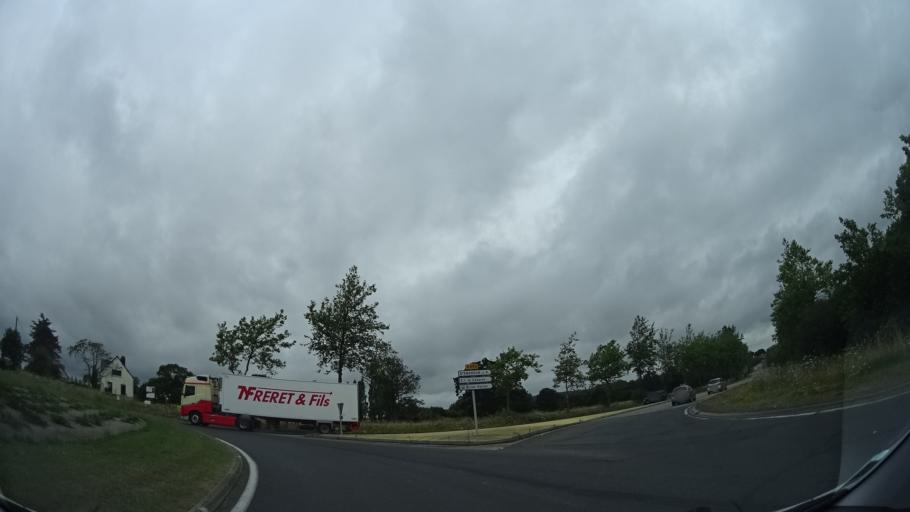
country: FR
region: Lower Normandy
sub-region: Departement de la Manche
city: La Haye-du-Puits
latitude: 49.2951
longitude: -1.5577
